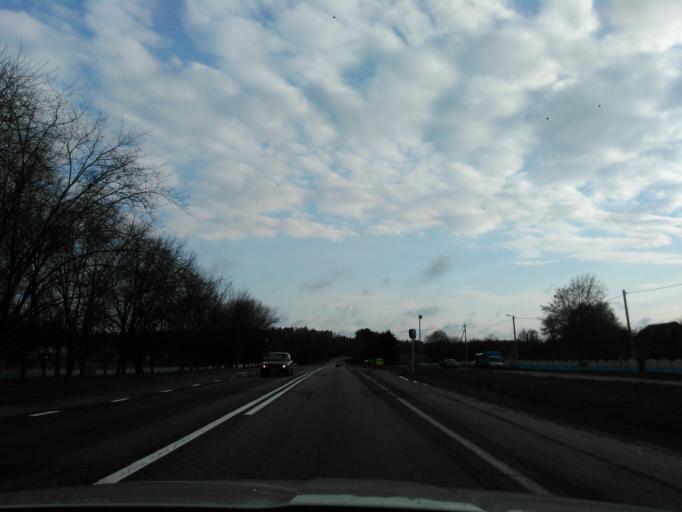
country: BY
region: Minsk
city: Lahoysk
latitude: 54.2919
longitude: 27.8726
